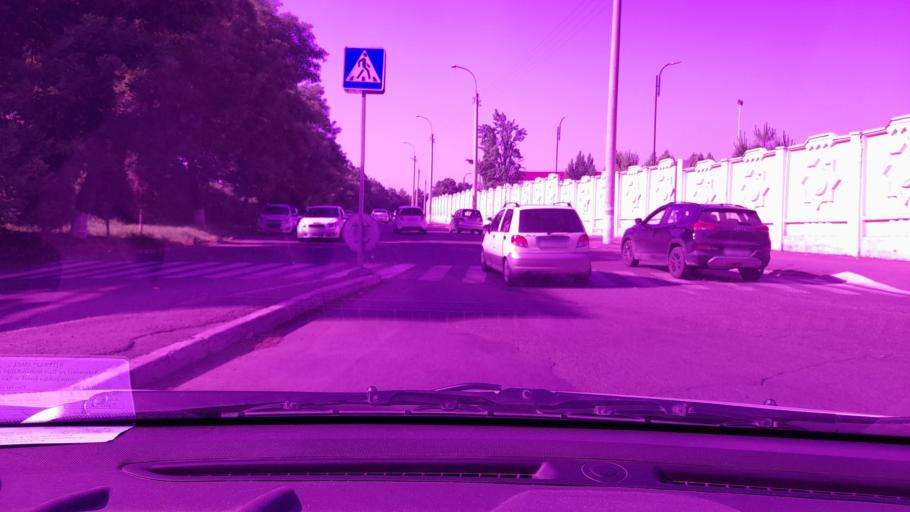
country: UZ
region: Toshkent
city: Salor
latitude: 41.3189
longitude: 69.3110
